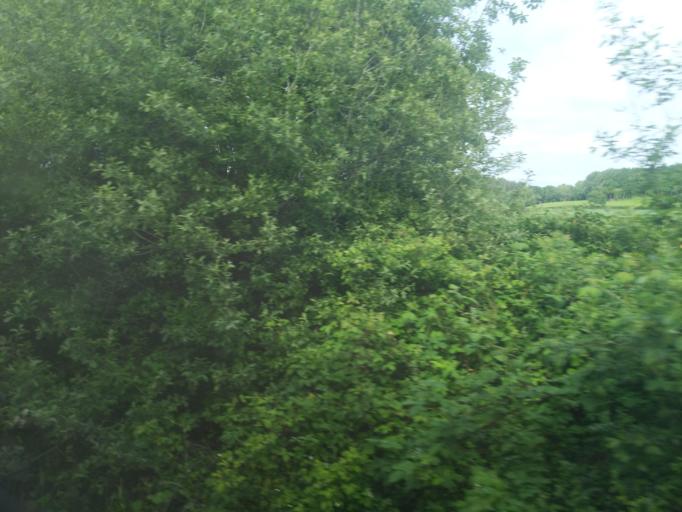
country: GB
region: England
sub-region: Devon
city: Barnstaple
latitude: 50.9957
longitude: -3.9828
